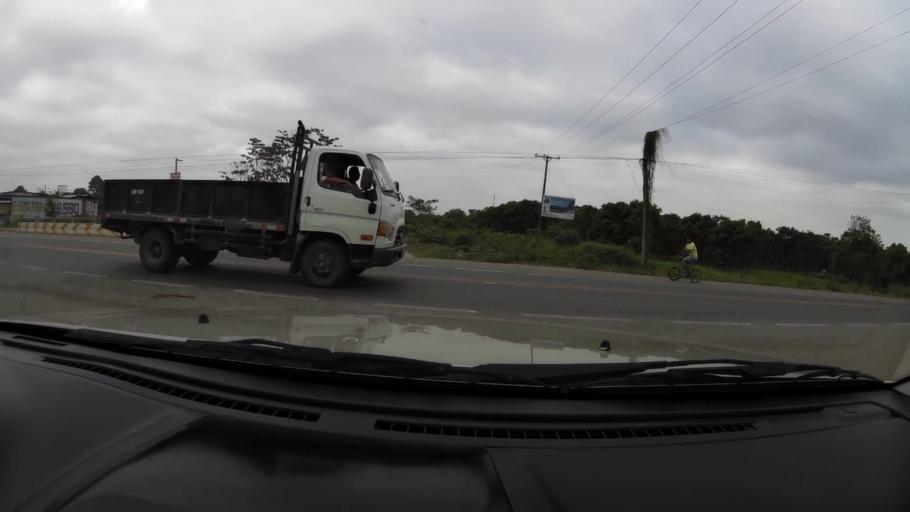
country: EC
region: Guayas
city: Yaguachi Nuevo
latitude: -2.2436
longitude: -79.6451
